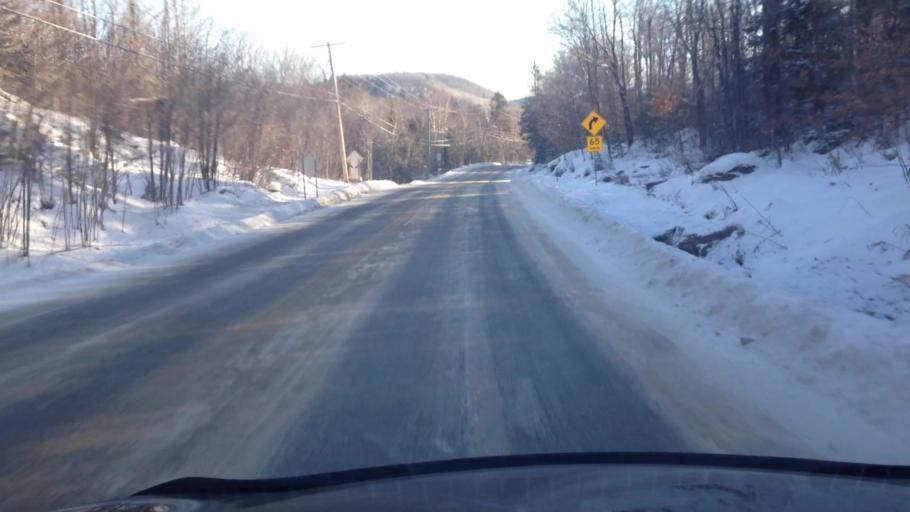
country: CA
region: Quebec
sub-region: Laurentides
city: Sainte-Agathe-des-Monts
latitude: 45.9362
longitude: -74.4435
